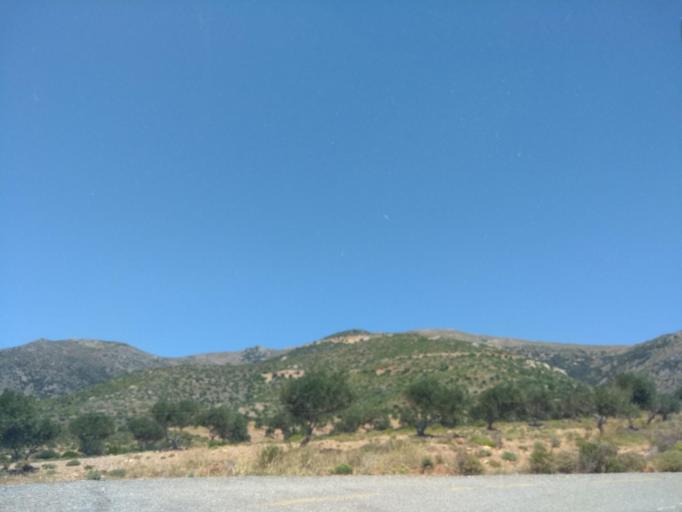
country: GR
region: Crete
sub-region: Nomos Chanias
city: Vryses
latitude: 35.3598
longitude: 23.5463
